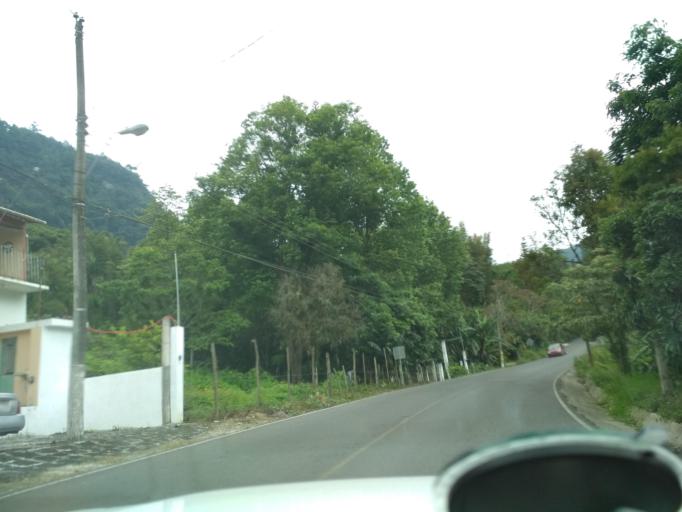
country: MX
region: Veracruz
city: Jilotepec
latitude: 19.6160
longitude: -96.9332
